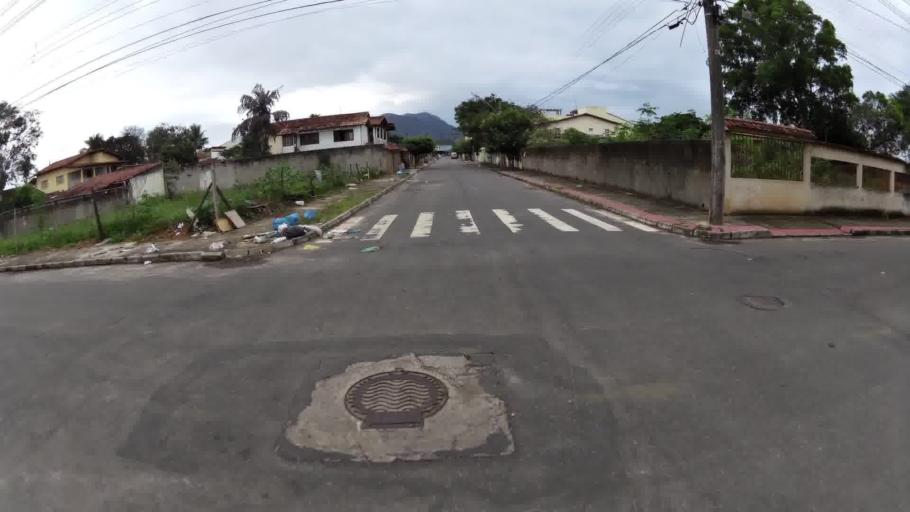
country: BR
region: Espirito Santo
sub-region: Guarapari
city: Guarapari
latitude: -20.6515
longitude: -40.4919
